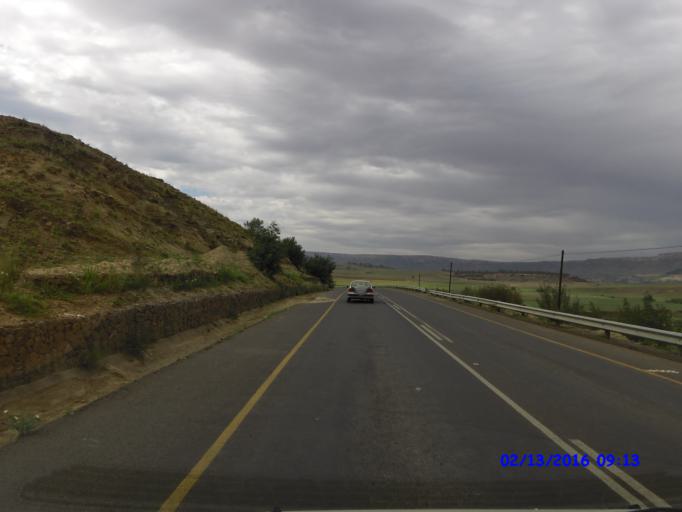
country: LS
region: Maseru
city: Maseru
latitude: -29.3841
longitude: 27.5035
